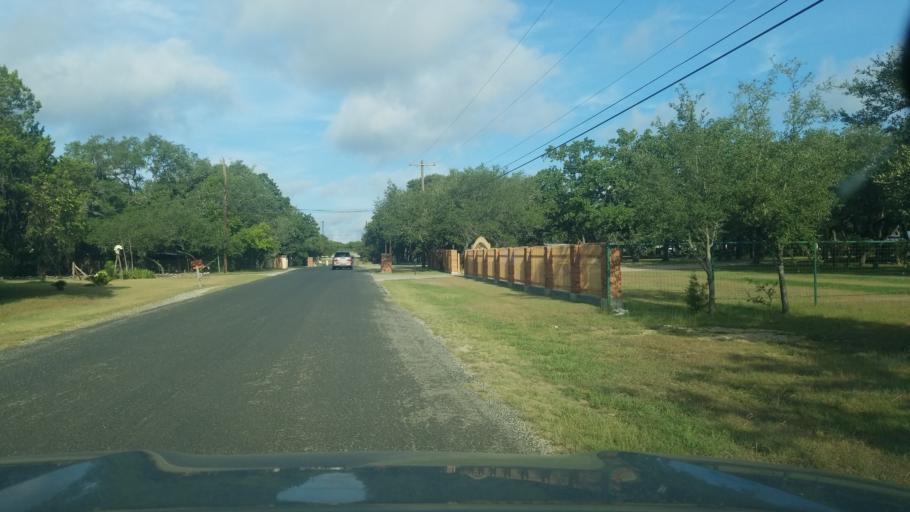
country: US
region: Texas
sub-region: Bexar County
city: Timberwood Park
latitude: 29.6953
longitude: -98.5183
